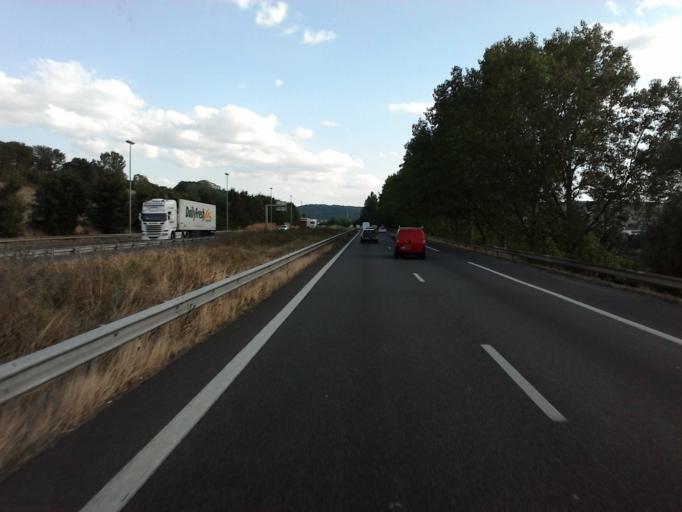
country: FR
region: Lorraine
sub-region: Departement de Meurthe-et-Moselle
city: Custines
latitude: 48.7759
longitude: 6.1441
